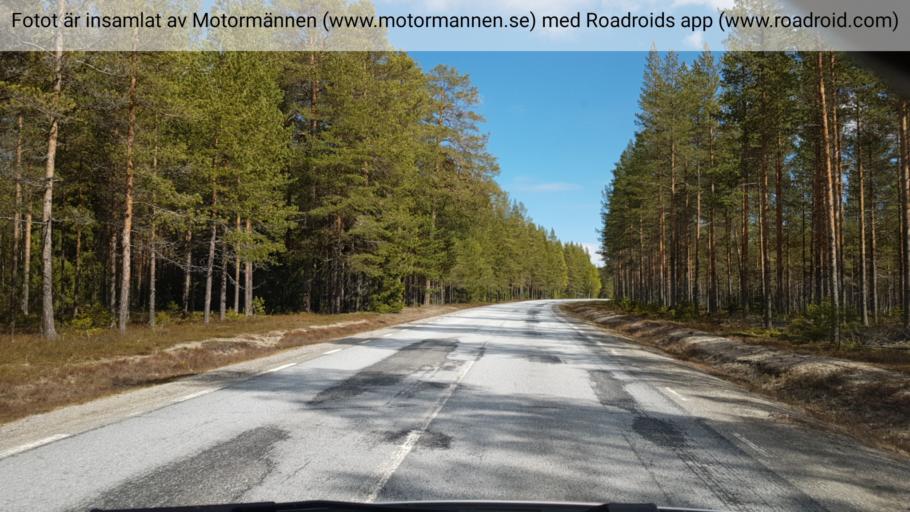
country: SE
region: Vaesterbotten
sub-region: Vindelns Kommun
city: Vindeln
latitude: 64.1657
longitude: 19.8020
